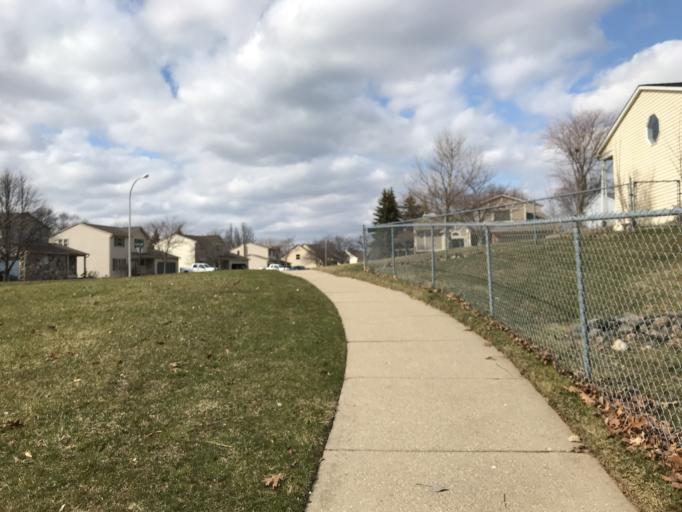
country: US
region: Michigan
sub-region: Oakland County
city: South Lyon
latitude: 42.4682
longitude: -83.6437
